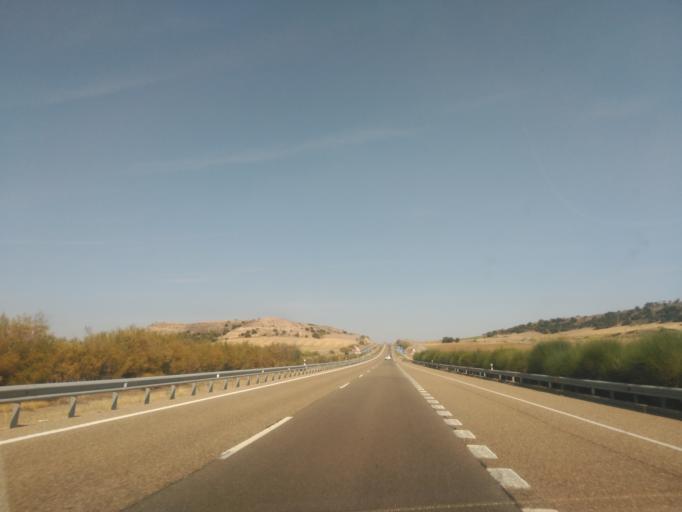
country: ES
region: Castille and Leon
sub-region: Provincia de Zamora
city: Canizal
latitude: 41.1967
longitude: -5.3458
